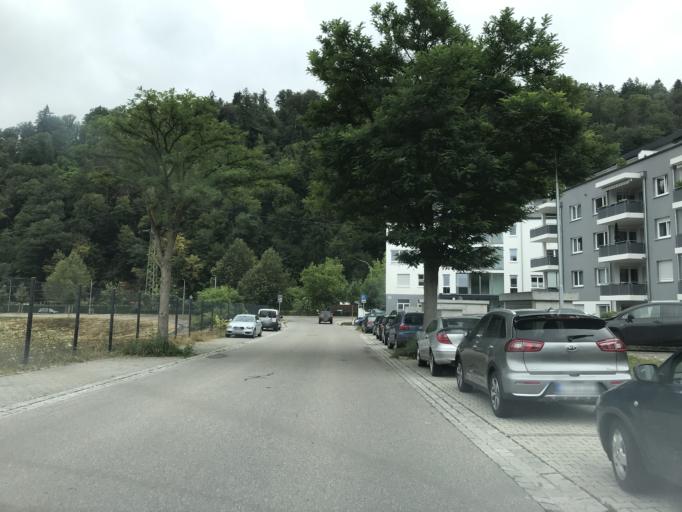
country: DE
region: Baden-Wuerttemberg
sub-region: Freiburg Region
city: Schopfheim
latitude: 47.6493
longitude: 7.8120
